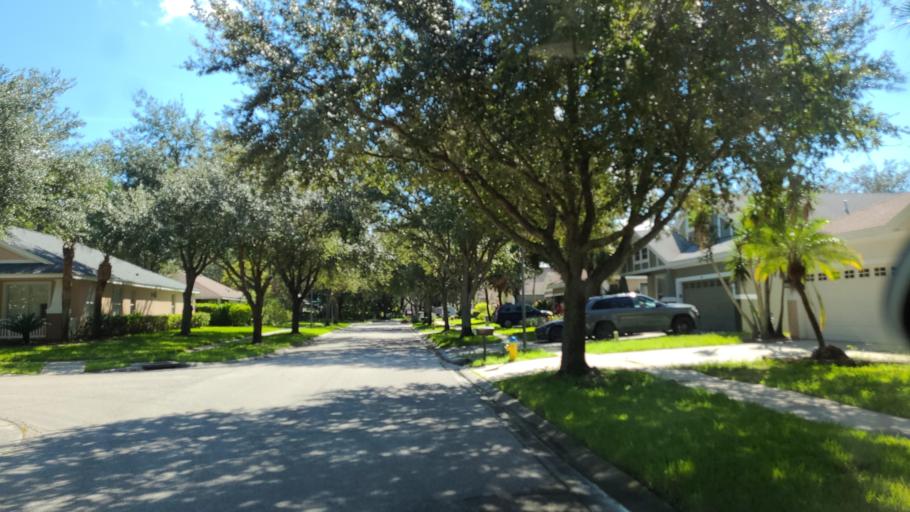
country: US
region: Florida
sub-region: Hillsborough County
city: Fish Hawk
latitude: 27.8409
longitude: -82.2274
